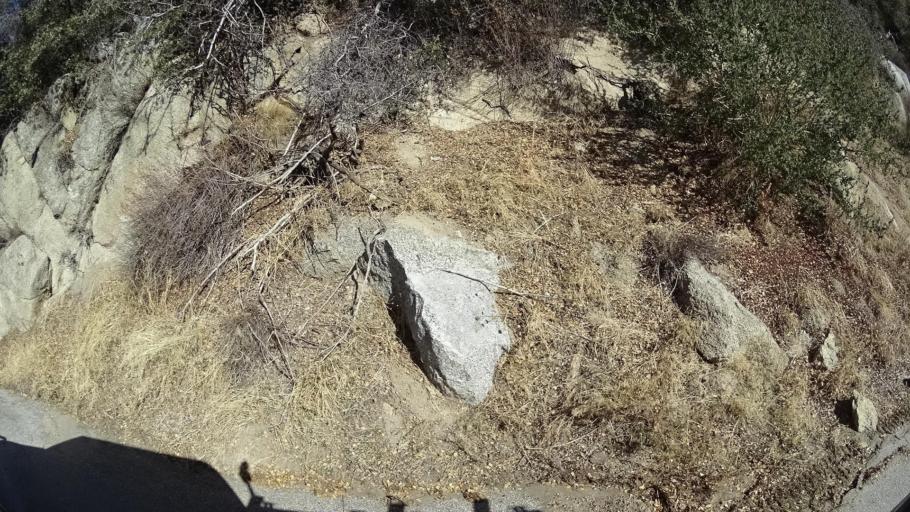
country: US
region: California
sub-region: Kern County
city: Bodfish
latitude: 35.4718
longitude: -118.6476
